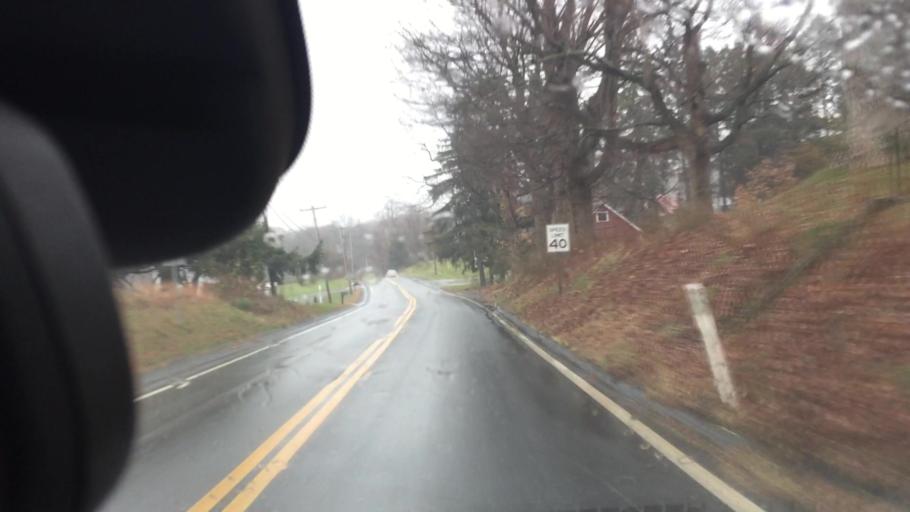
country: US
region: Massachusetts
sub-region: Hampden County
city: Granville
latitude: 42.1747
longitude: -72.9157
